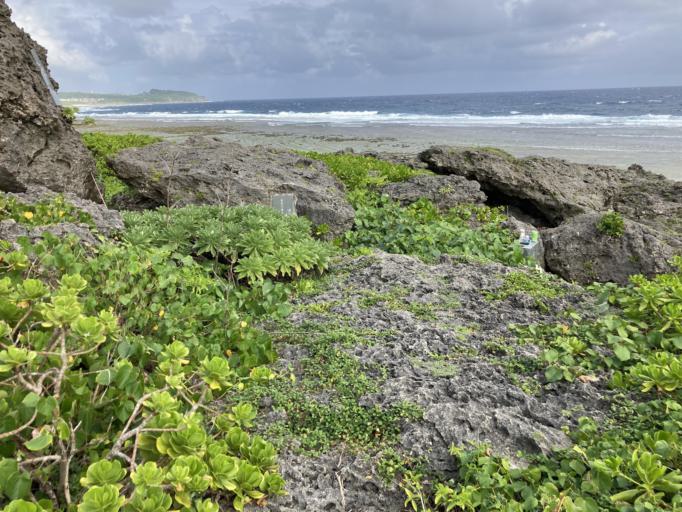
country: JP
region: Okinawa
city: Itoman
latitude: 26.0779
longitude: 127.6827
